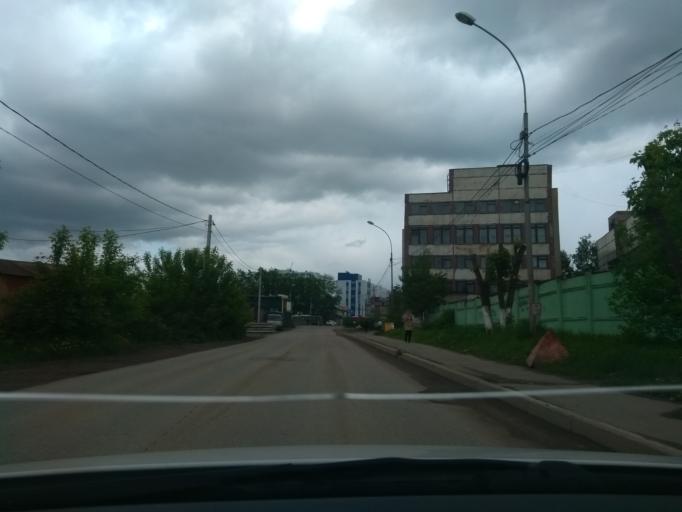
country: RU
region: Perm
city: Perm
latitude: 57.9814
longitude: 56.2415
